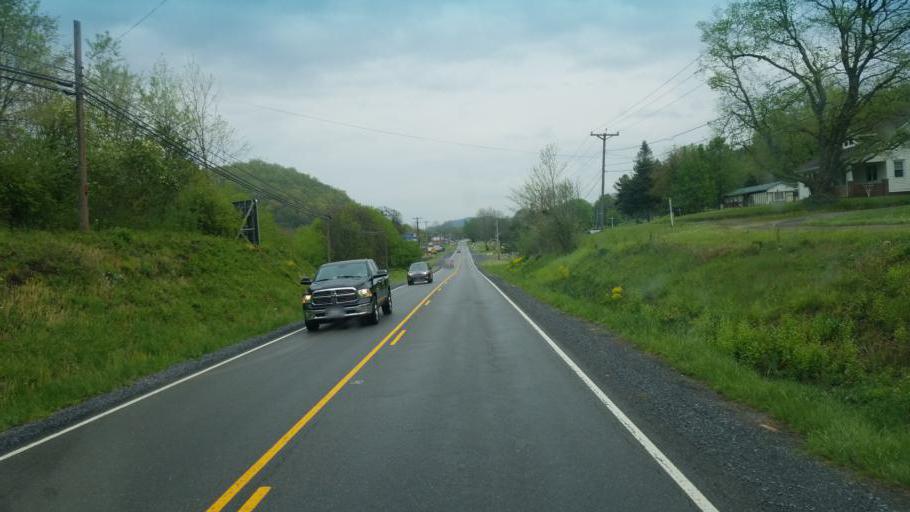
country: US
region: Virginia
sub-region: Smyth County
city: Atkins
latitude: 36.8633
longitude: -81.4442
